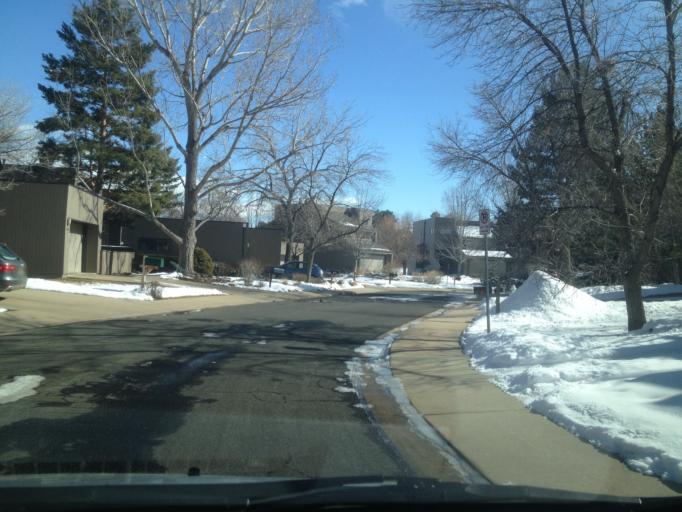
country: US
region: Colorado
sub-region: Boulder County
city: Boulder
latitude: 40.0474
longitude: -105.2913
